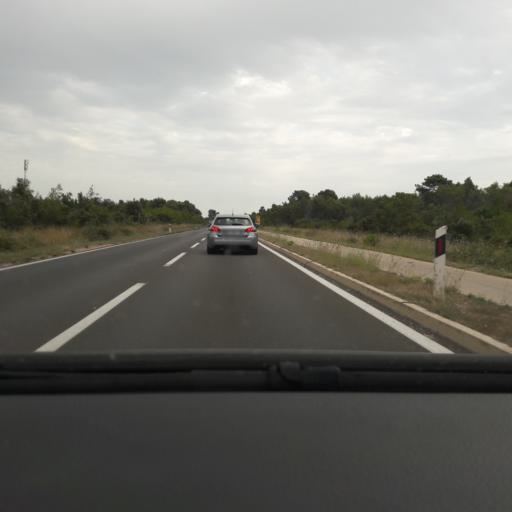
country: HR
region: Zadarska
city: Nin
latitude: 44.1802
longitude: 15.1878
